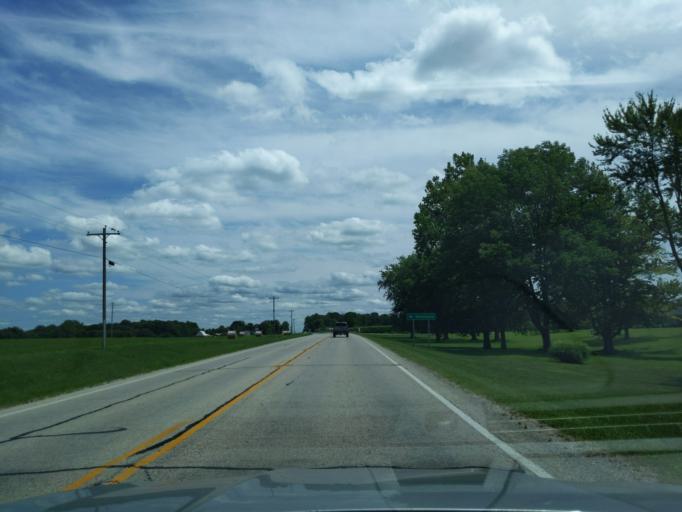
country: US
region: Indiana
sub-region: Ripley County
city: Batesville
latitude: 39.3087
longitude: -85.2950
